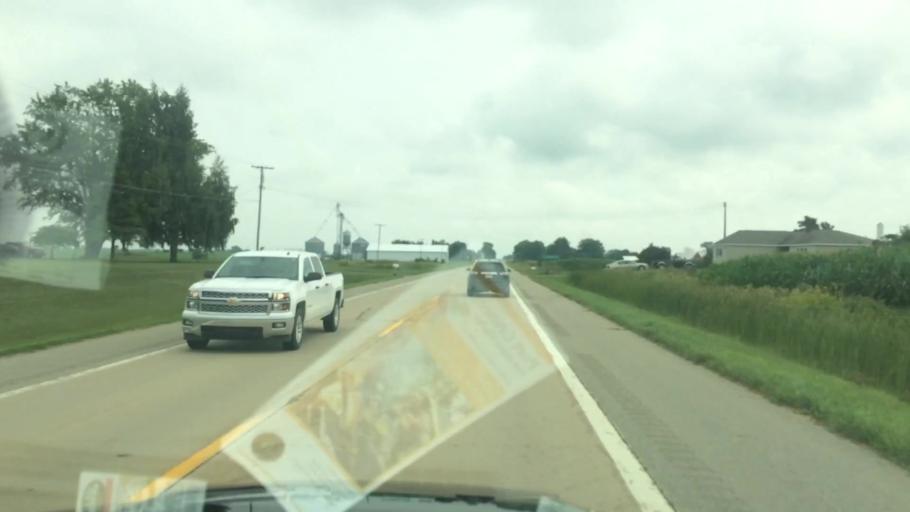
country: US
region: Michigan
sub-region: Huron County
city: Bad Axe
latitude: 44.0422
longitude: -82.9542
